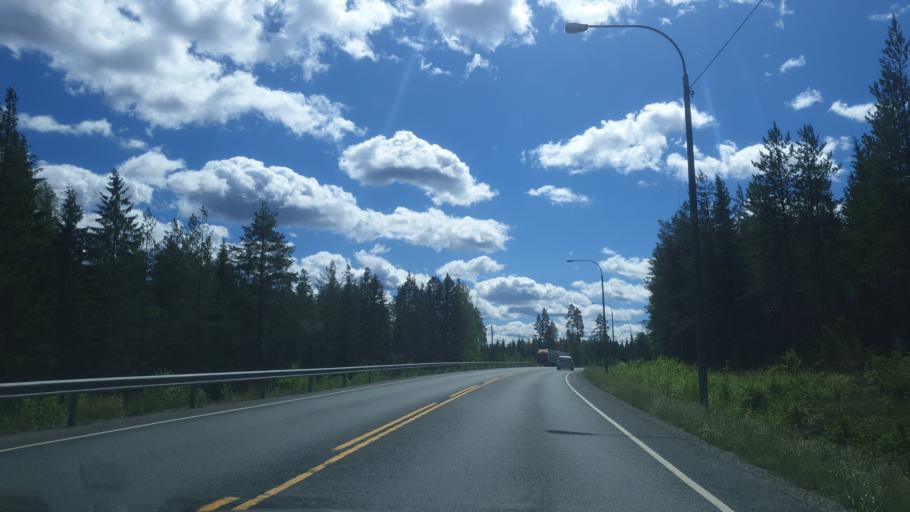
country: FI
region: Northern Savo
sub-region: Varkaus
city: Leppaevirta
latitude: 62.6271
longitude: 27.6205
